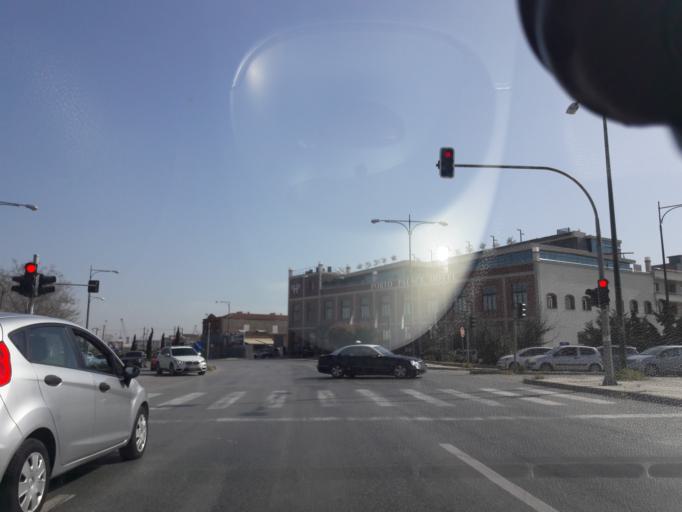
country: GR
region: Central Macedonia
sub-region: Nomos Thessalonikis
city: Ampelokipoi
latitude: 40.6440
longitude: 22.9099
